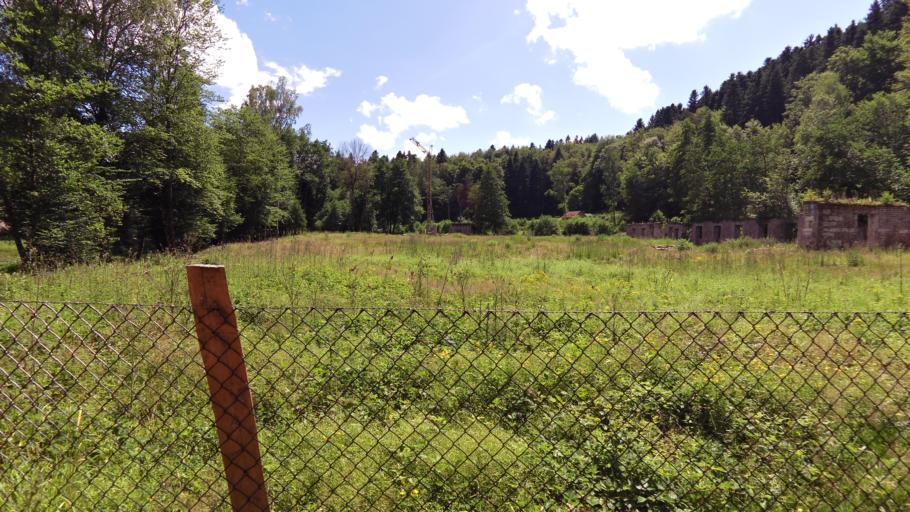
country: FR
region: Lorraine
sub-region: Departement de la Moselle
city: Walscheid
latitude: 48.6237
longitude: 7.1280
